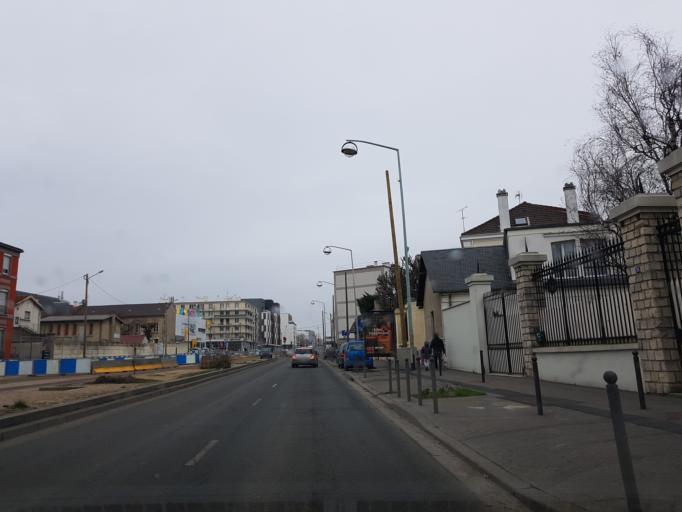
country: FR
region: Ile-de-France
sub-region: Departement du Val-de-Marne
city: Vitry-sur-Seine
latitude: 48.7935
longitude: 2.3859
